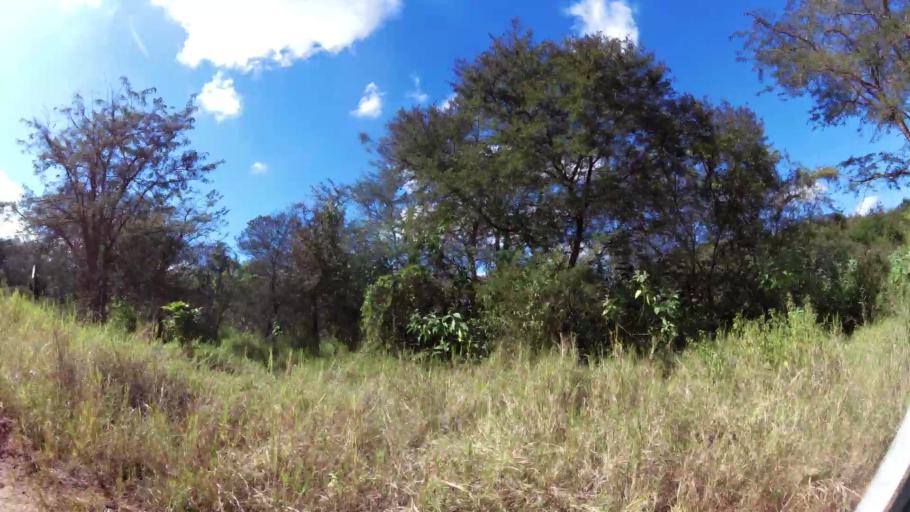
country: ZA
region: Limpopo
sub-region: Mopani District Municipality
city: Tzaneen
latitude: -23.8046
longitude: 30.1677
